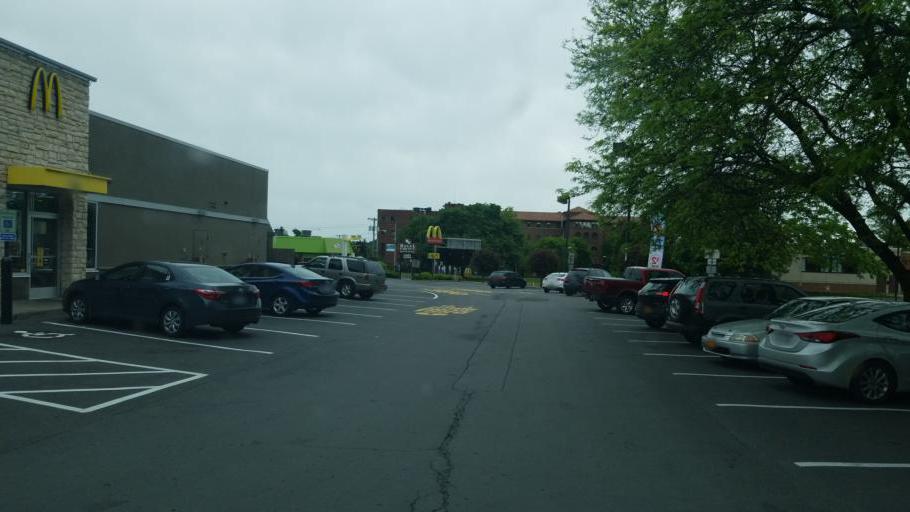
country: US
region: New York
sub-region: Oneida County
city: Utica
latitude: 43.0891
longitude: -75.2569
